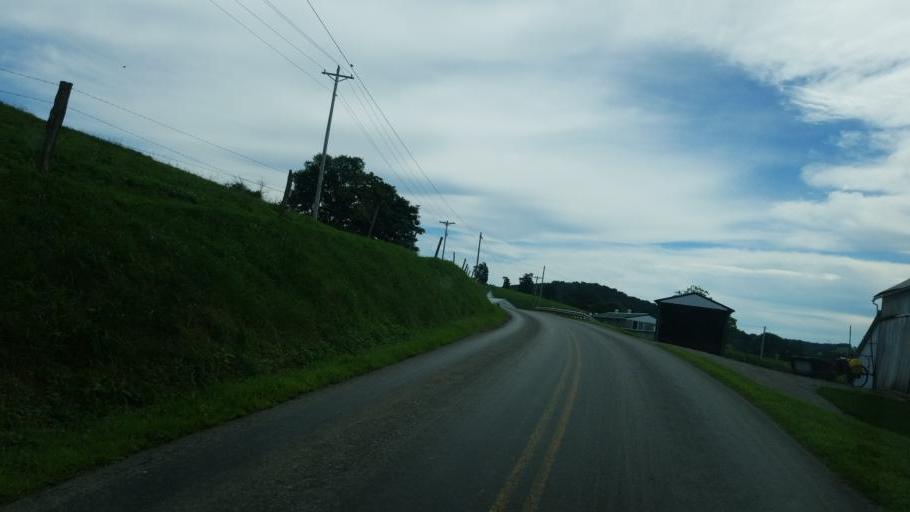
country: US
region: Ohio
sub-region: Holmes County
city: Millersburg
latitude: 40.4772
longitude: -81.8387
